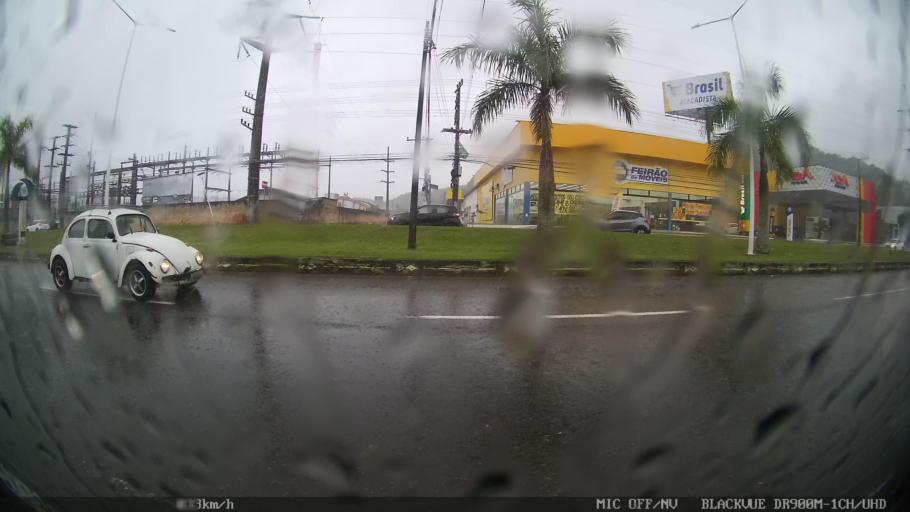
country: BR
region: Santa Catarina
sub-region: Balneario Camboriu
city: Balneario Camboriu
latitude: -26.9470
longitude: -48.6405
